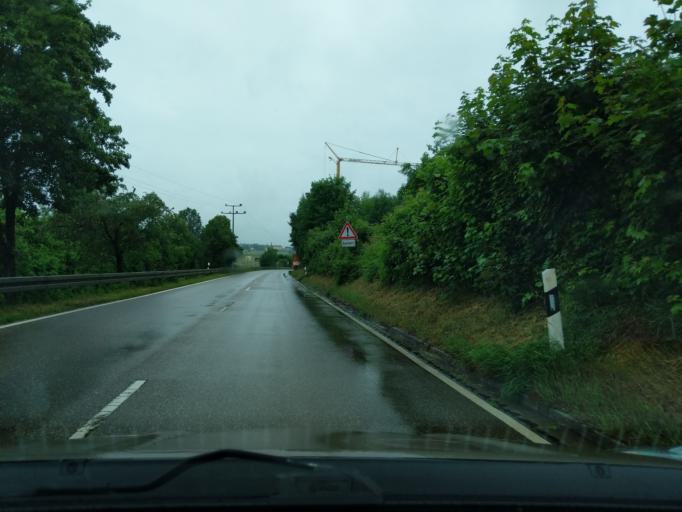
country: DE
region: Bavaria
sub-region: Upper Palatinate
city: Sinzing
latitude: 49.0303
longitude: 12.0346
